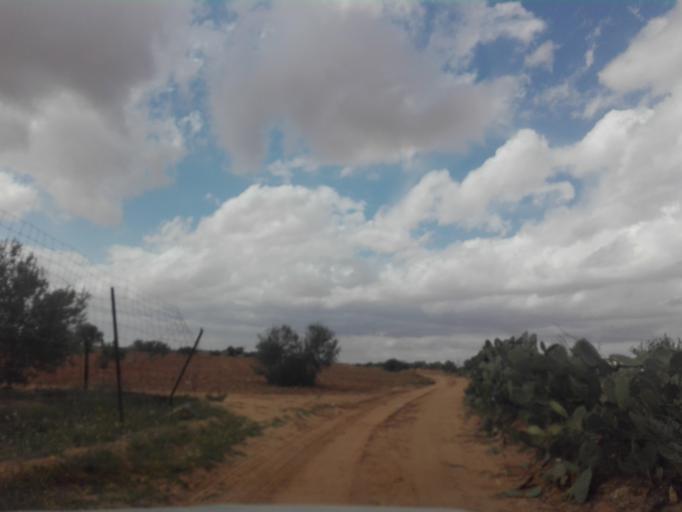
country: TN
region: Safaqis
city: Sfax
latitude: 34.6959
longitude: 10.4454
